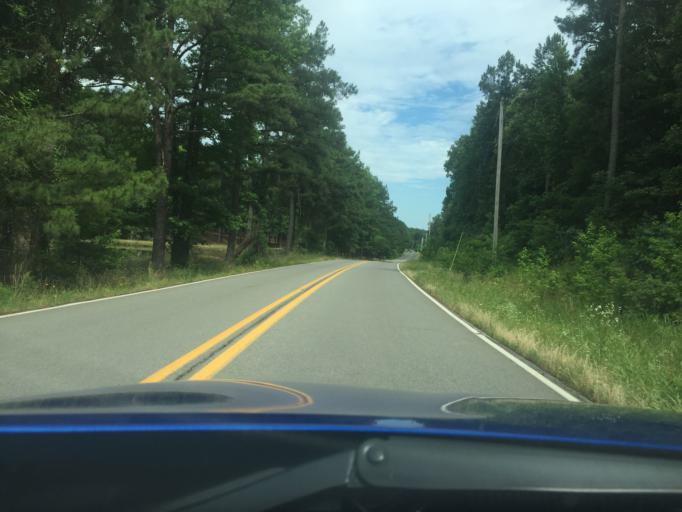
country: US
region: Arkansas
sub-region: Pulaski County
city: Maumelle
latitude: 34.8348
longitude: -92.4557
